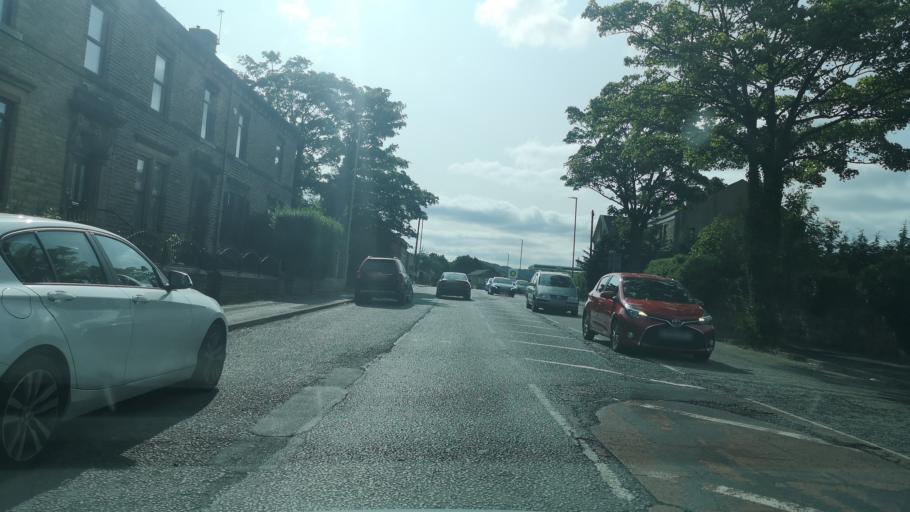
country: GB
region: England
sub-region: Kirklees
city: Dewsbury
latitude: 53.6827
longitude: -1.6334
